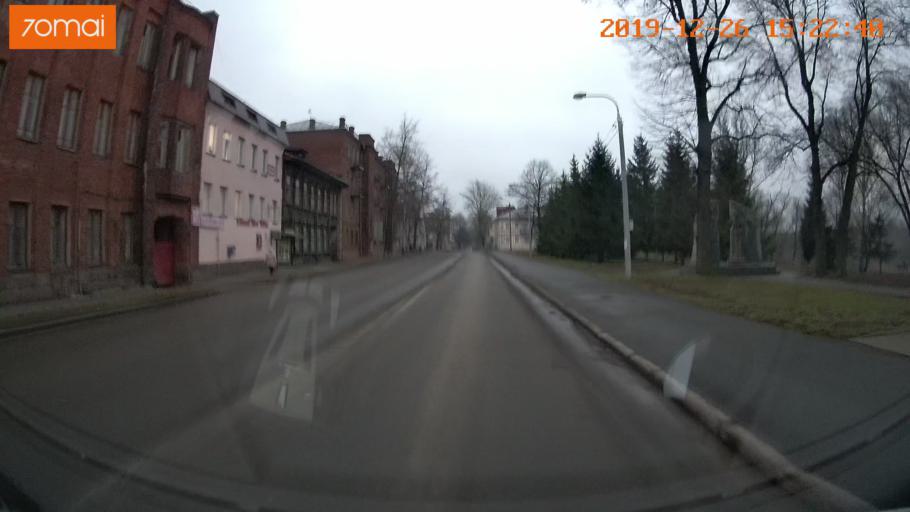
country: RU
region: Jaroslavl
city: Rybinsk
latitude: 58.0475
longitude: 38.8597
